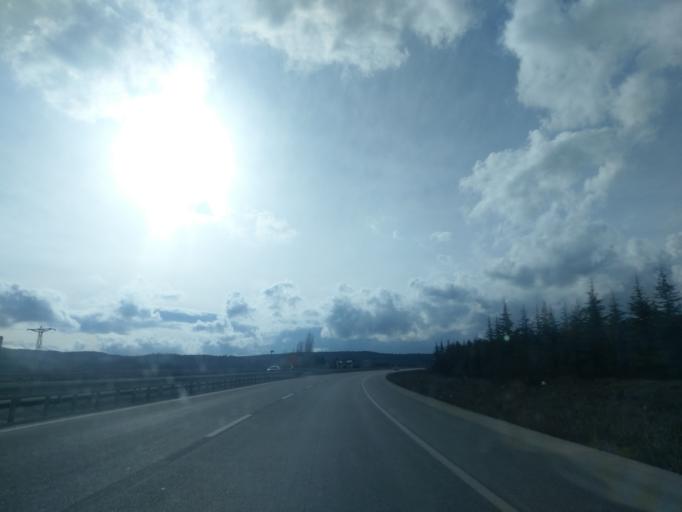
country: TR
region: Kuetahya
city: Sabuncu
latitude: 39.5723
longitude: 30.1152
